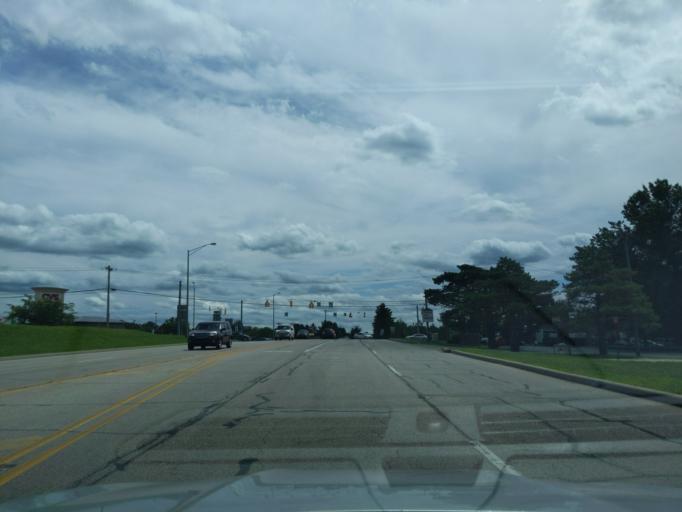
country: US
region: Indiana
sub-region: Ripley County
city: Batesville
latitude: 39.3067
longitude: -85.2190
